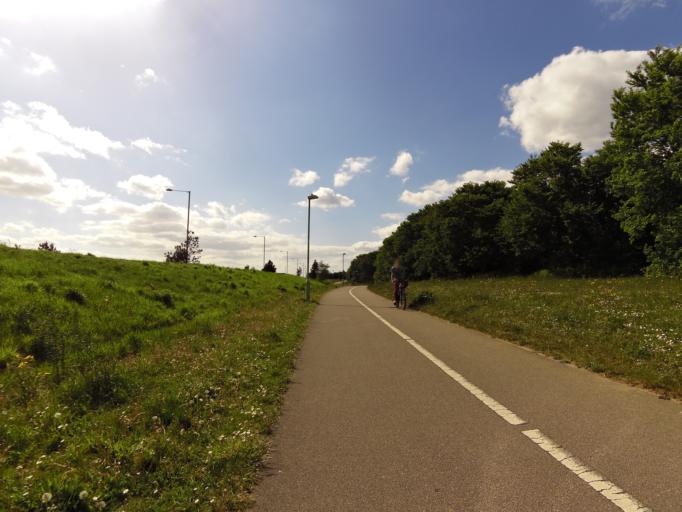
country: GB
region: England
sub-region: Suffolk
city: Kessingland
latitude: 52.4547
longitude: 1.7029
